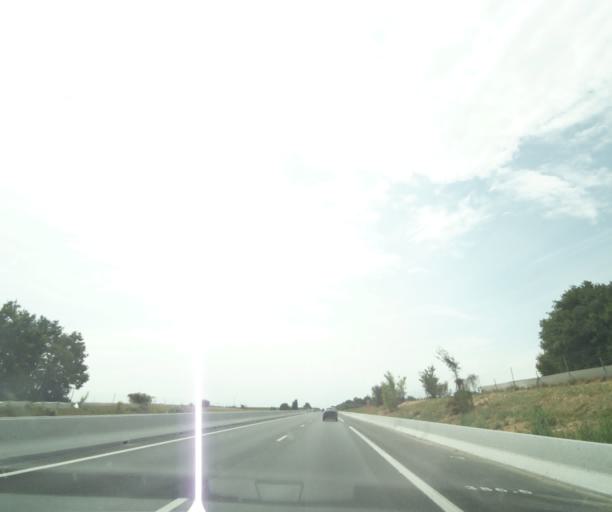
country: FR
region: Poitou-Charentes
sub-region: Departement des Deux-Sevres
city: Beauvoir-sur-Niort
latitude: 46.1906
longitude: -0.4895
